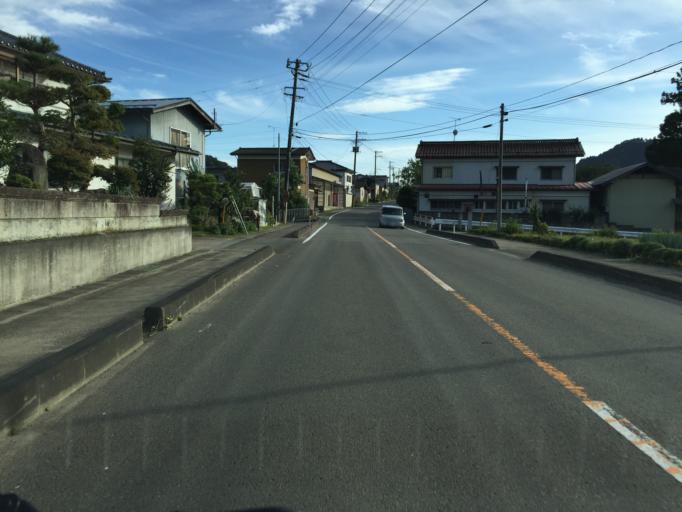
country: JP
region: Fukushima
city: Yanagawamachi-saiwaicho
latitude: 37.8175
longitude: 140.6199
